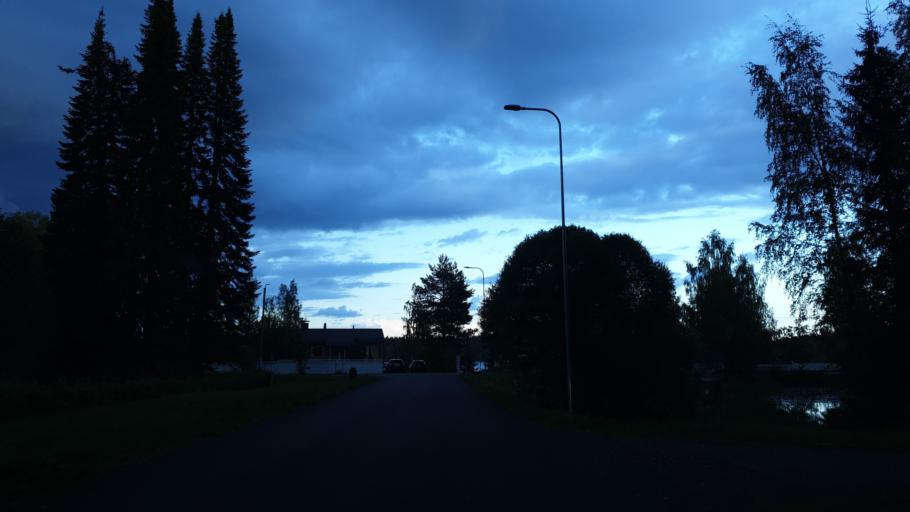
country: FI
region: Northern Savo
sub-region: Varkaus
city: Leppaevirta
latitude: 62.5835
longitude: 27.6181
